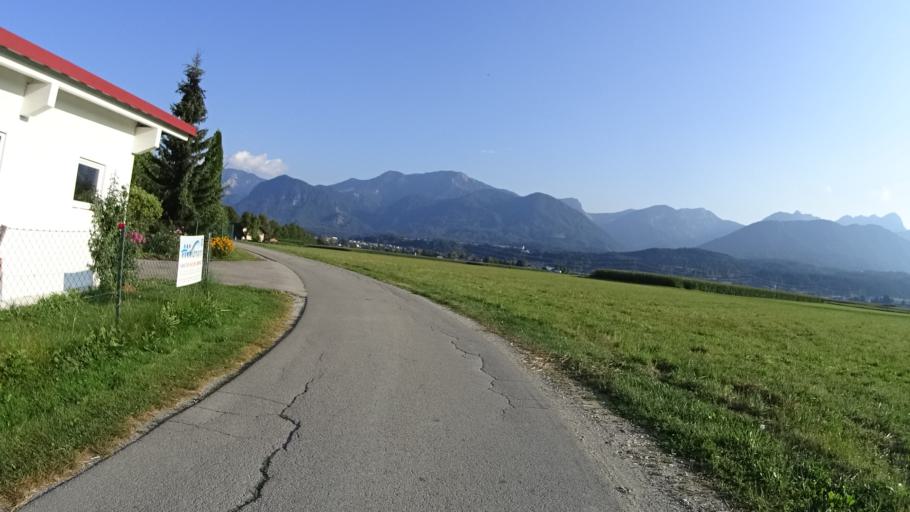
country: AT
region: Carinthia
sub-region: Politischer Bezirk Villach Land
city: Sankt Jakob
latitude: 46.5664
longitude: 14.0568
